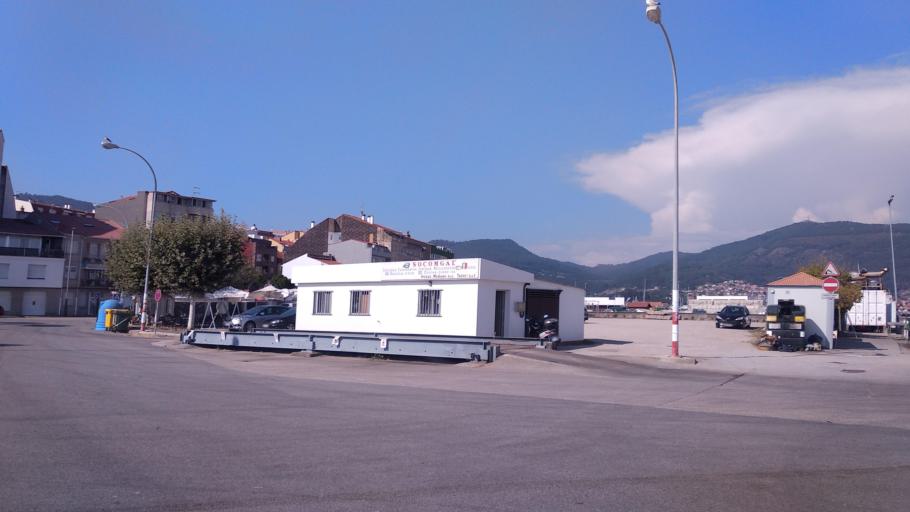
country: ES
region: Galicia
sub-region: Provincia de Pontevedra
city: Moana
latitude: 42.2738
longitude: -8.7366
